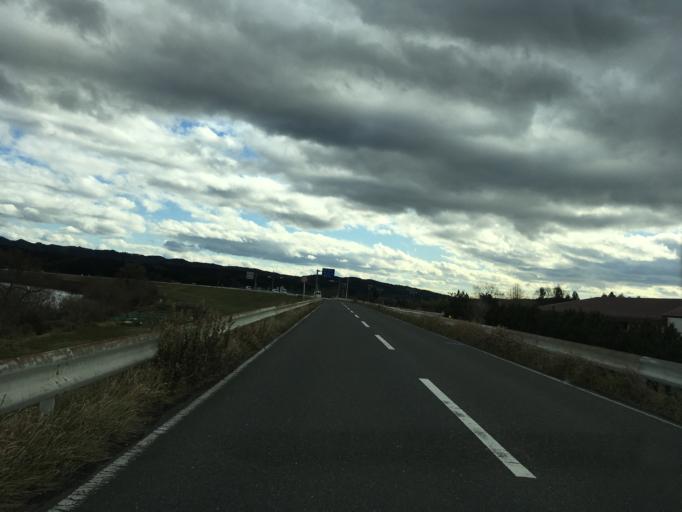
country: JP
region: Miyagi
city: Wakuya
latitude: 38.7090
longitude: 141.2668
